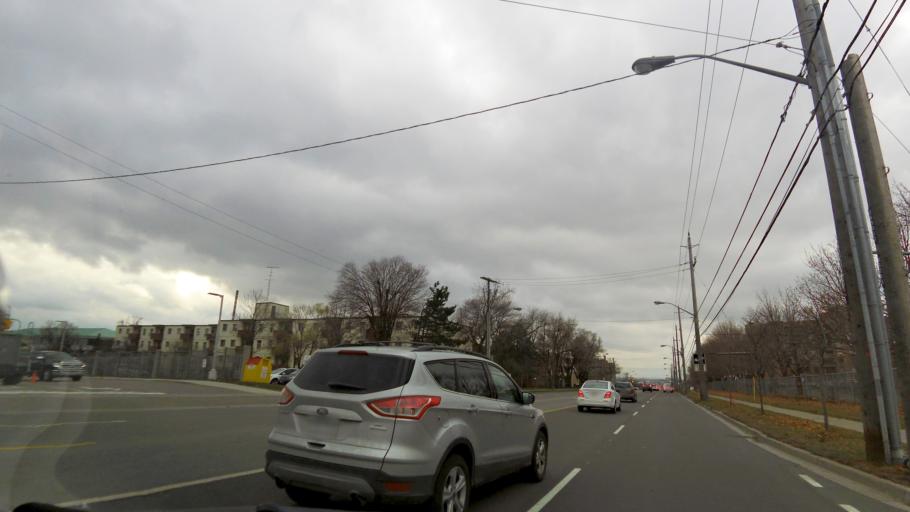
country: CA
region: Ontario
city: Concord
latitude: 43.7246
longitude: -79.4915
